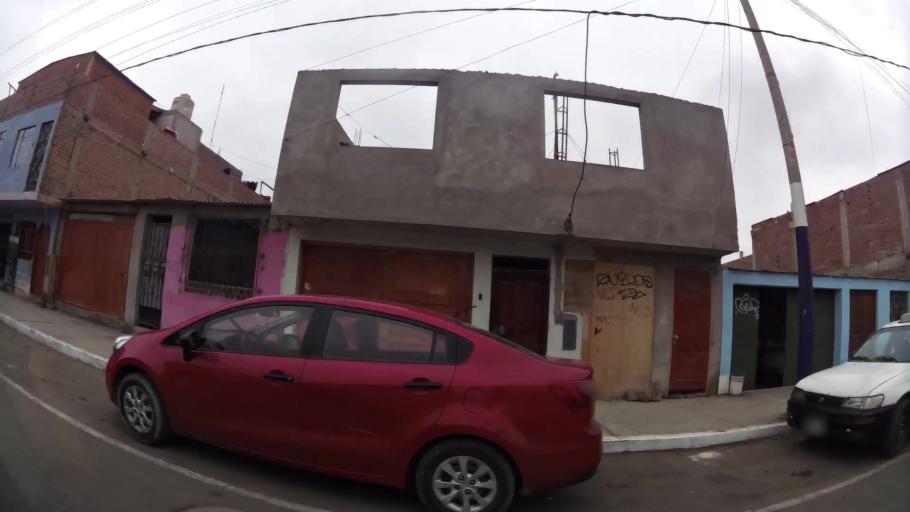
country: PE
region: Lima
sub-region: Lima
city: Surco
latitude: -12.1975
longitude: -76.9964
